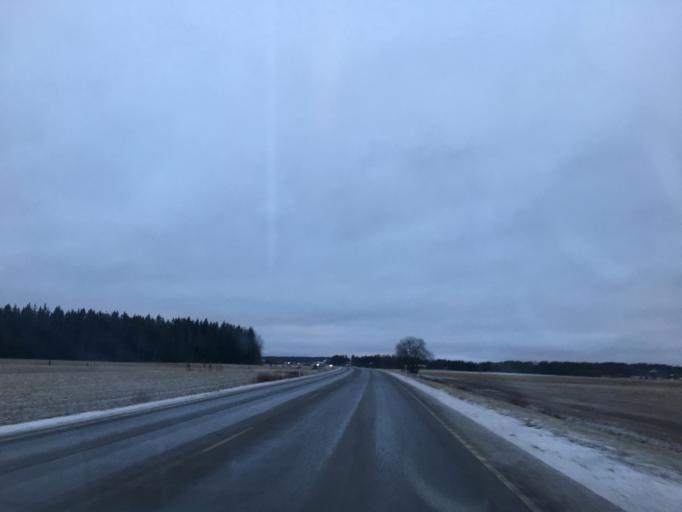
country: FI
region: Varsinais-Suomi
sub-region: Loimaa
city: Aura
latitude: 60.6593
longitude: 22.5587
